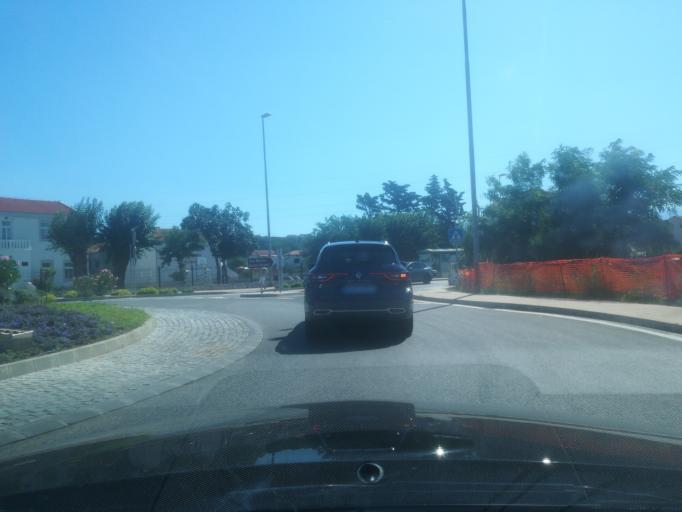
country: HR
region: Primorsko-Goranska
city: Lopar
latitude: 44.8298
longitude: 14.7312
